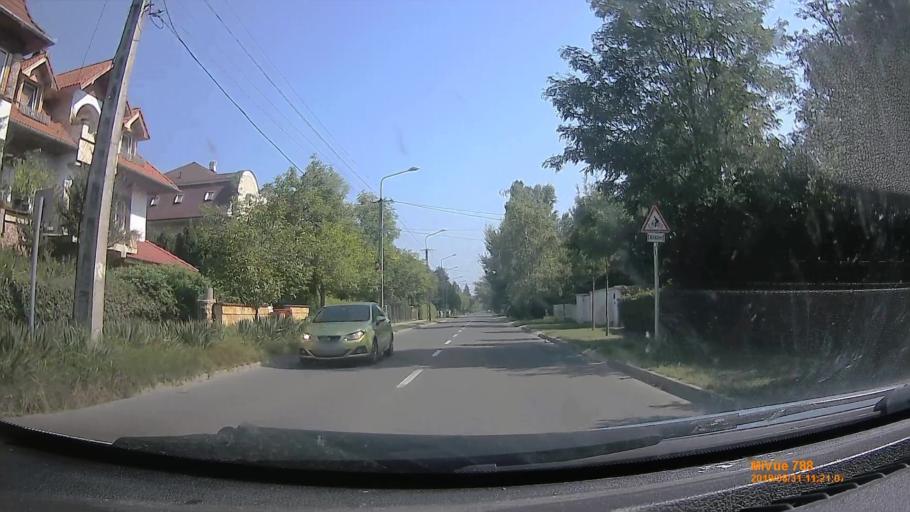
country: HU
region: Somogy
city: Siofok
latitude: 46.9201
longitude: 18.0855
